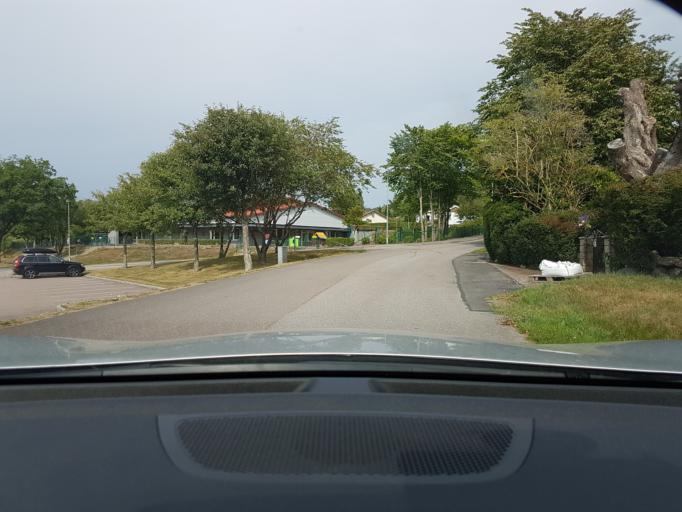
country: SE
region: Vaestra Goetaland
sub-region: Ale Kommun
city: Surte
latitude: 57.8483
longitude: 12.0207
